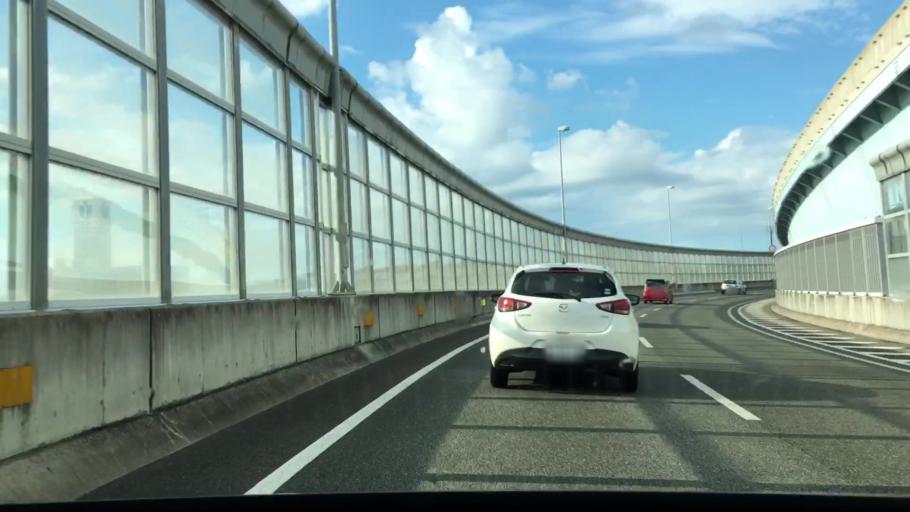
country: JP
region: Fukuoka
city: Fukuoka-shi
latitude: 33.5762
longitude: 130.3158
